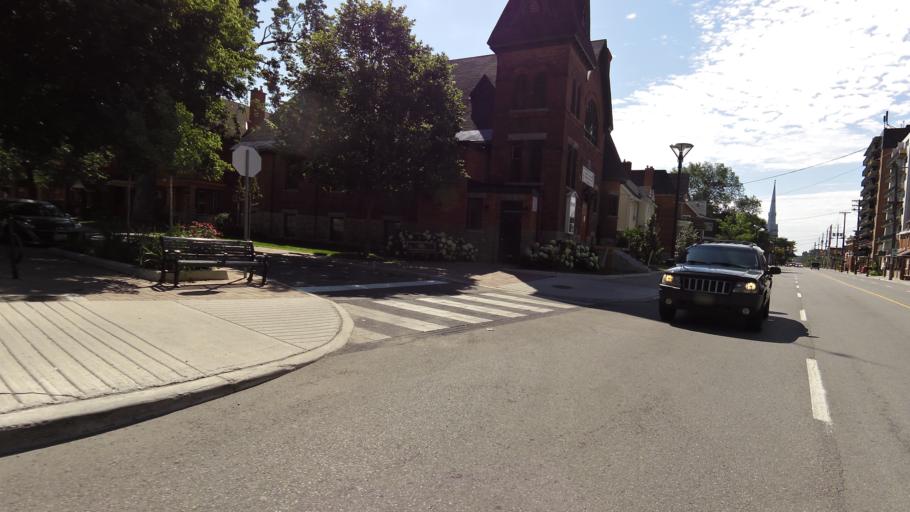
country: CA
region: Ontario
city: Ottawa
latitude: 45.4130
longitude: -75.7066
